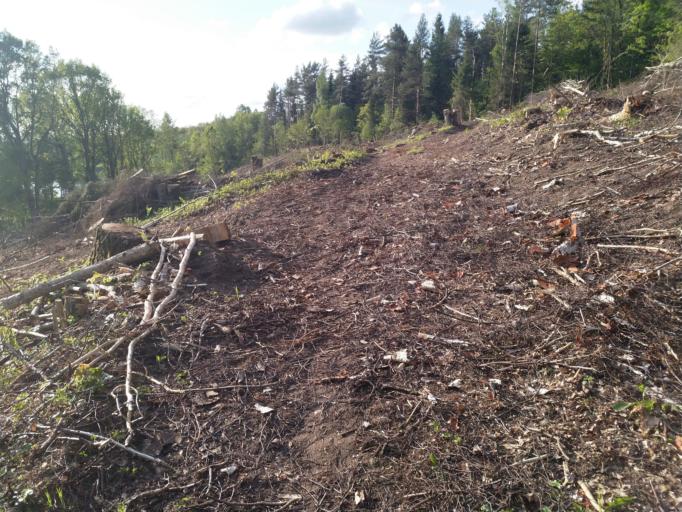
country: LV
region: Kuldigas Rajons
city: Kuldiga
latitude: 56.8593
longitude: 21.8592
